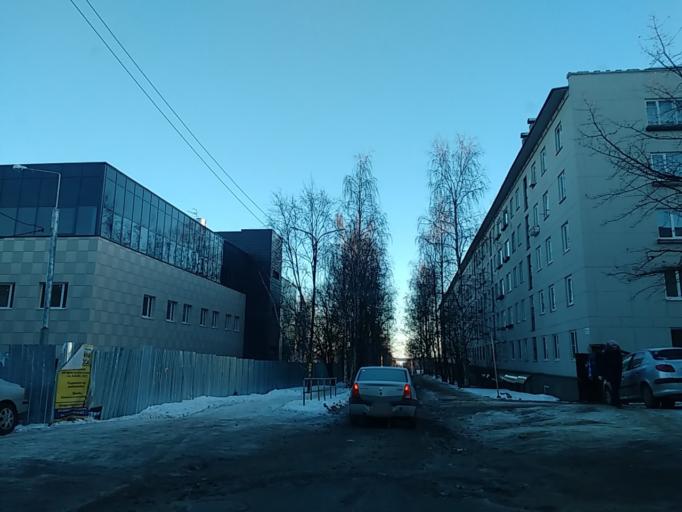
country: RU
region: Republic of Karelia
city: Petrozavodsk
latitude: 61.7796
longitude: 34.3712
